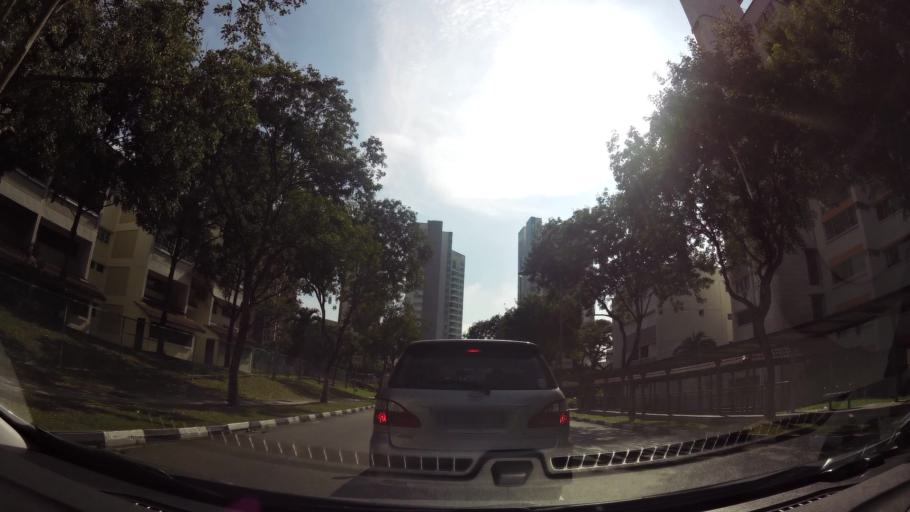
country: SG
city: Singapore
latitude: 1.3513
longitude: 103.8390
